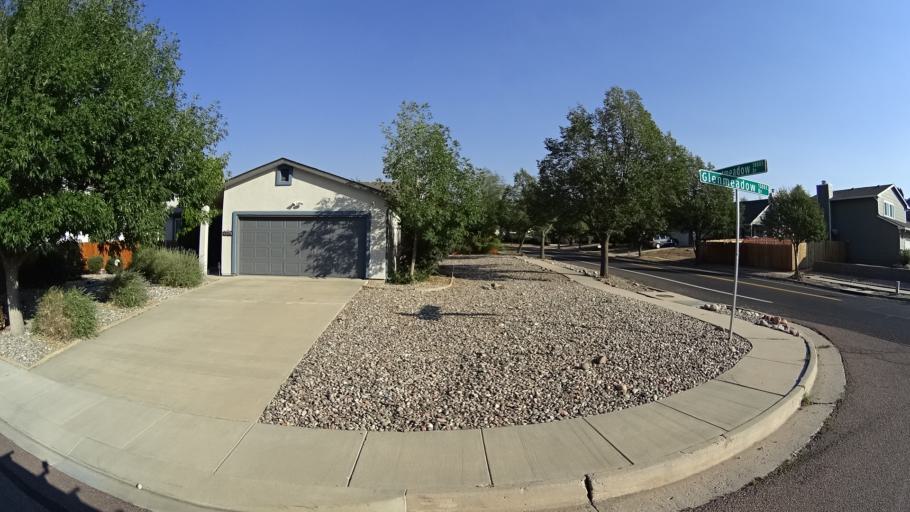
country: US
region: Colorado
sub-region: El Paso County
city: Stratmoor
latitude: 38.7772
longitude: -104.8040
